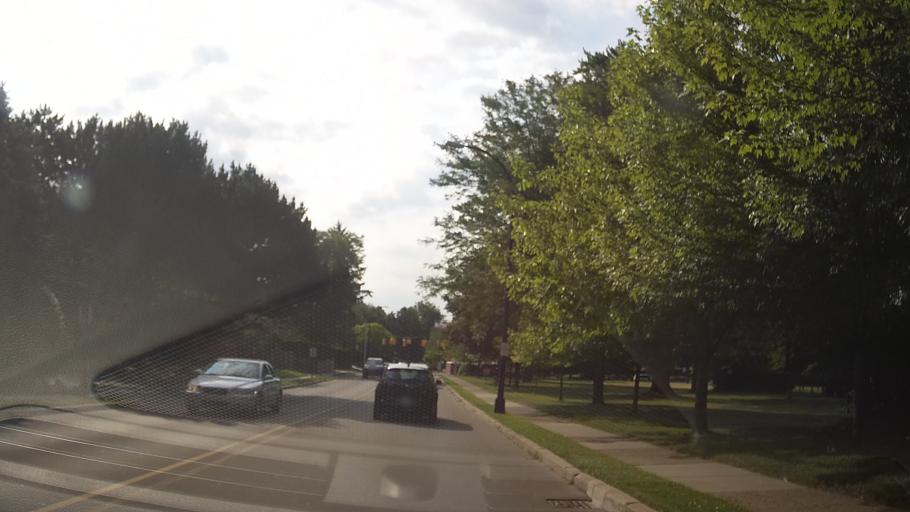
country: US
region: Michigan
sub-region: Wayne County
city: Grosse Pointe Farms
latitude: 42.4078
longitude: -82.8882
